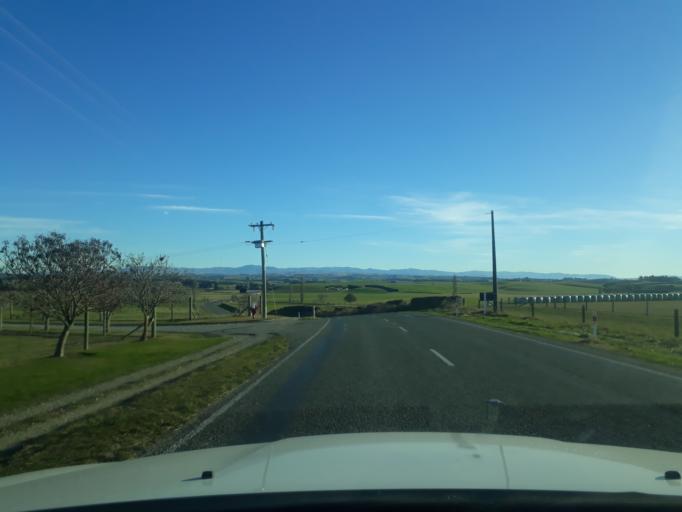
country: NZ
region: Canterbury
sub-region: Timaru District
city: Timaru
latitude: -44.3365
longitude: 171.2182
